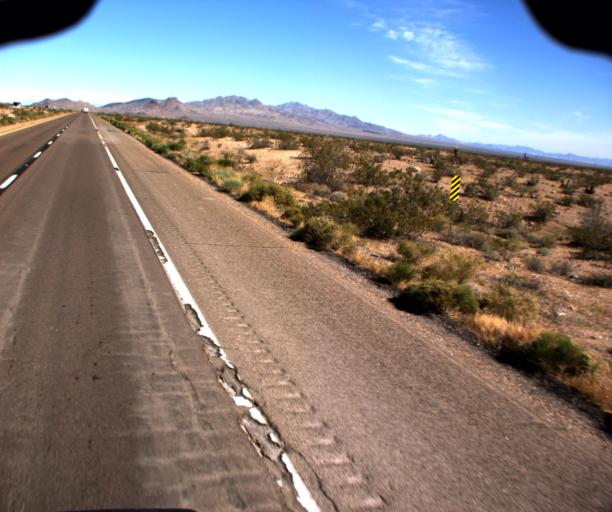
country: US
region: Arizona
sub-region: Mohave County
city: Dolan Springs
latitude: 35.8002
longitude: -114.5346
